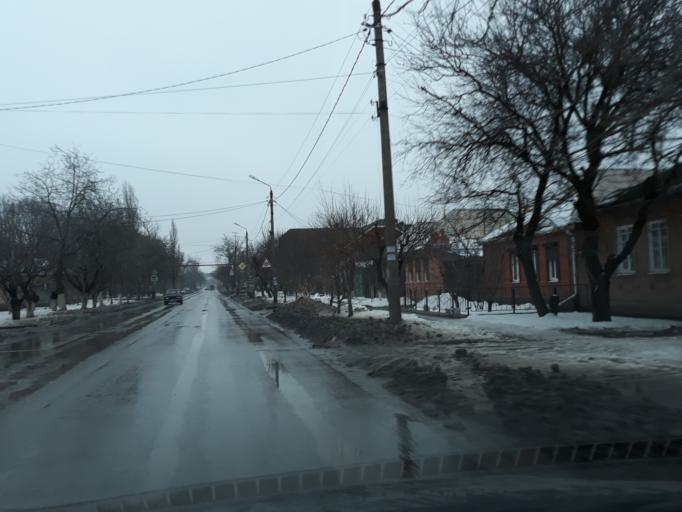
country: RU
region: Rostov
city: Taganrog
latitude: 47.2399
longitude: 38.8770
